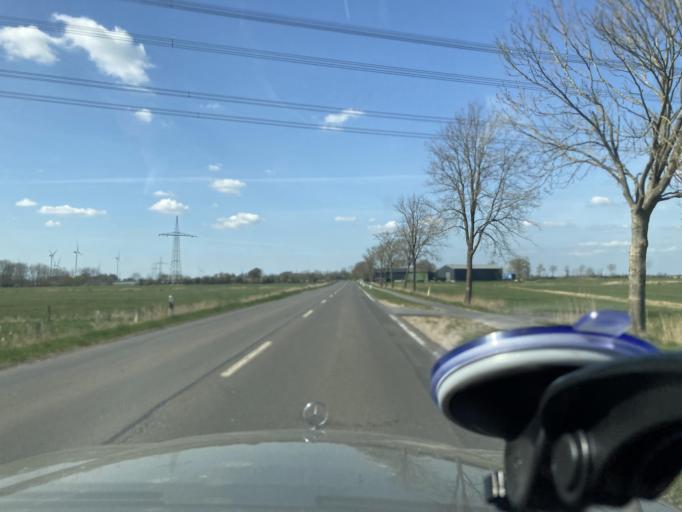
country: DE
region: Schleswig-Holstein
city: Weddingstedt
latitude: 54.2424
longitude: 9.0785
